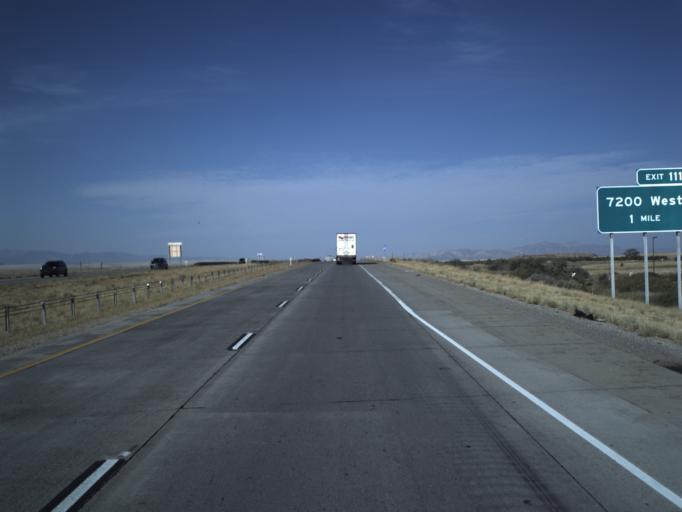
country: US
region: Utah
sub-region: Salt Lake County
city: West Valley City
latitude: 40.7712
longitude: -112.0362
